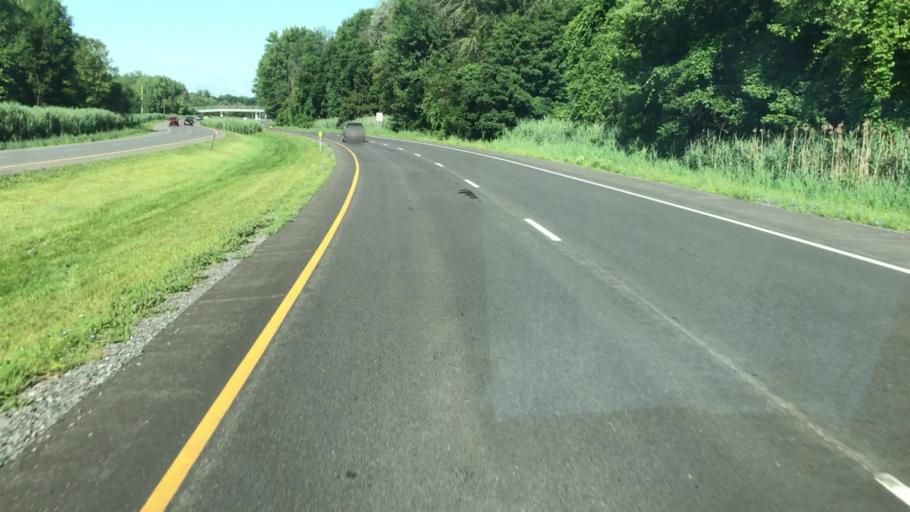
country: US
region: New York
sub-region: Onondaga County
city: Liverpool
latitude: 43.1316
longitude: -76.2314
